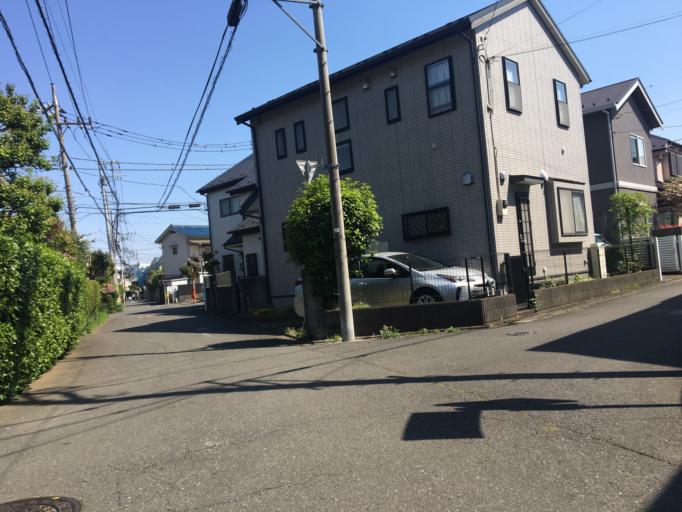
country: JP
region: Tokyo
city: Kokubunji
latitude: 35.7133
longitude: 139.4702
